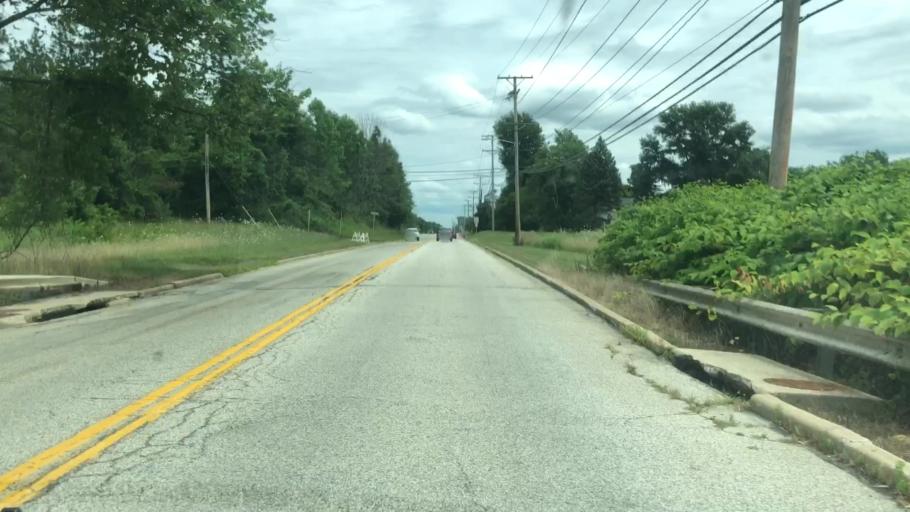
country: US
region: Ohio
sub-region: Summit County
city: Peninsula
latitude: 41.1809
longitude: -81.5566
